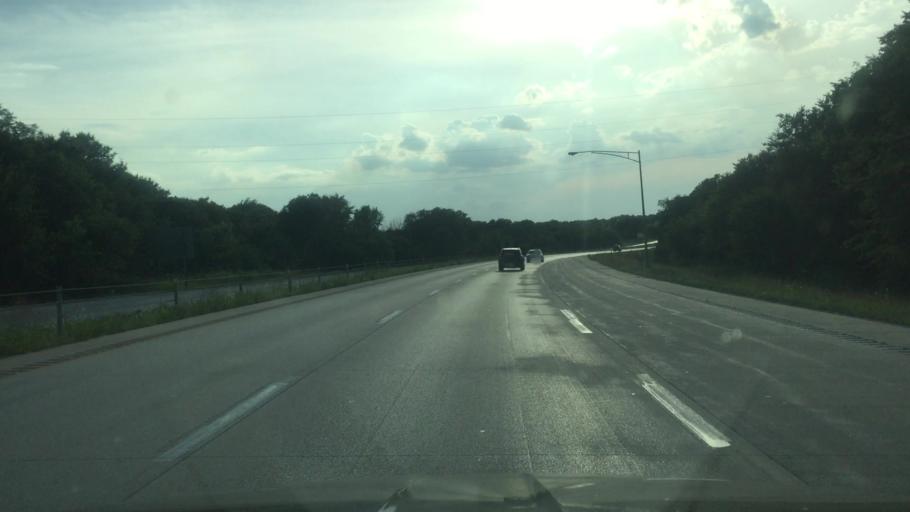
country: US
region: Missouri
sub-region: Jackson County
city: Lone Jack
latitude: 38.8683
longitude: -94.1775
